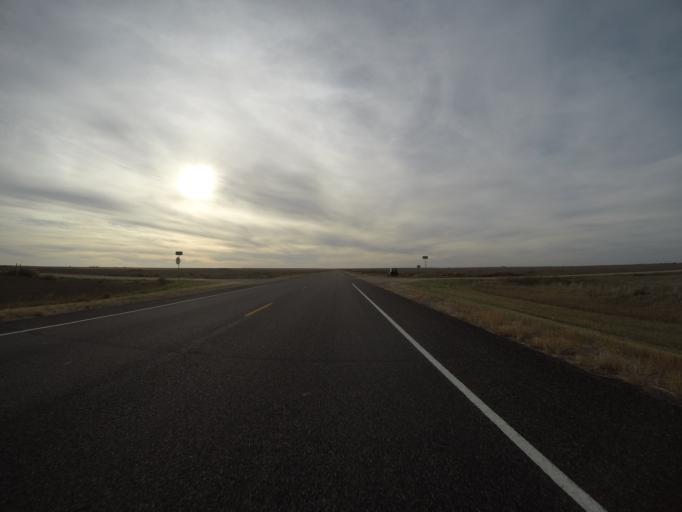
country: US
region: Kansas
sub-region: Cheyenne County
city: Saint Francis
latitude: 39.7463
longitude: -102.1054
